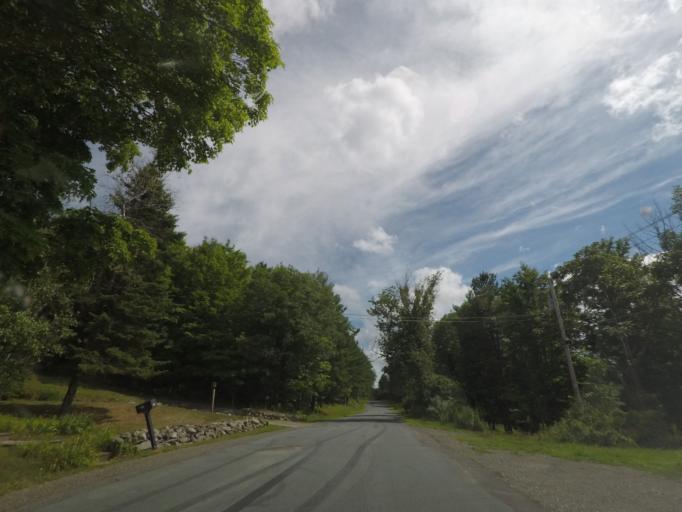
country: US
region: New York
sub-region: Rensselaer County
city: Poestenkill
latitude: 42.6730
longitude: -73.5500
